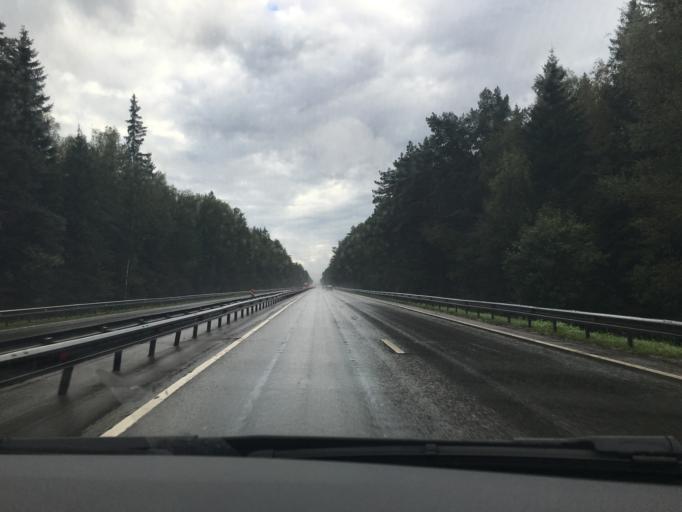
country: RU
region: Kaluga
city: Obninsk
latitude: 55.0273
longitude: 36.5723
